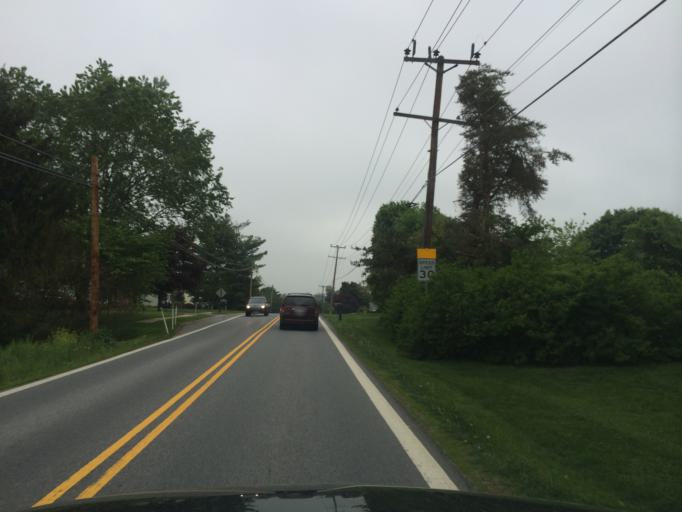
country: US
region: Maryland
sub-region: Carroll County
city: Eldersburg
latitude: 39.3846
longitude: -76.9214
